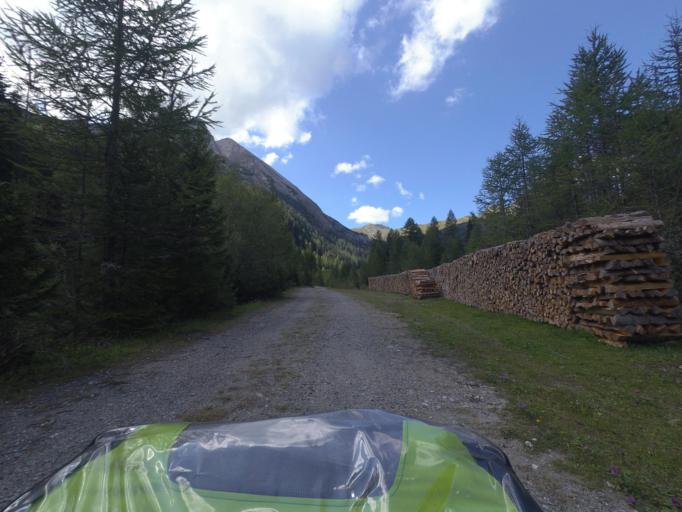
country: AT
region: Salzburg
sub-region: Politischer Bezirk Tamsweg
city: Zederhaus
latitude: 47.1864
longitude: 13.4039
